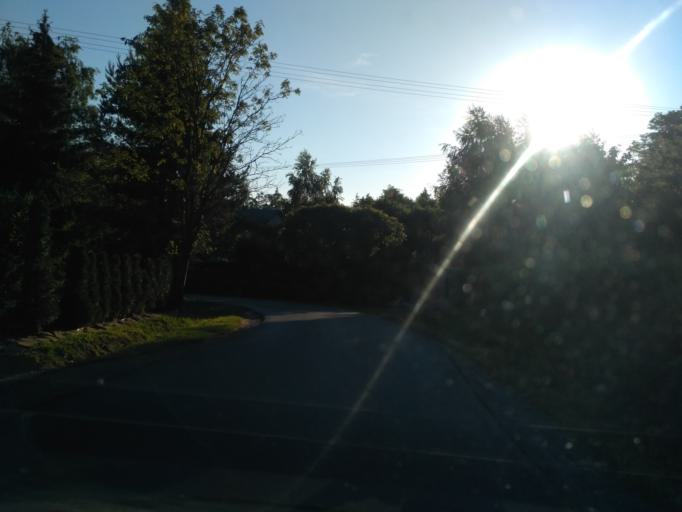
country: PL
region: Subcarpathian Voivodeship
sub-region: Powiat rzeszowski
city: Lubenia
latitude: 49.9138
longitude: 21.9150
